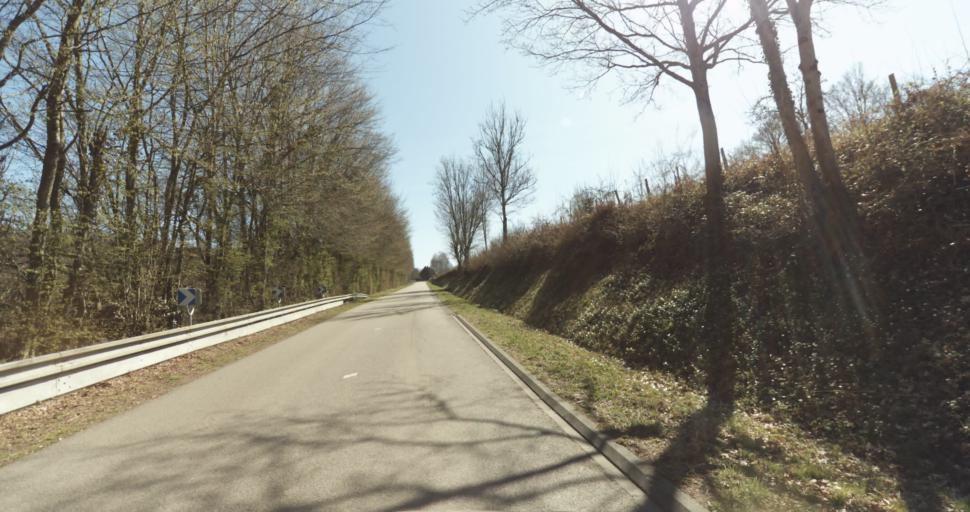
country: FR
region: Lower Normandy
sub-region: Departement du Calvados
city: Livarot
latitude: 48.9704
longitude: 0.0694
